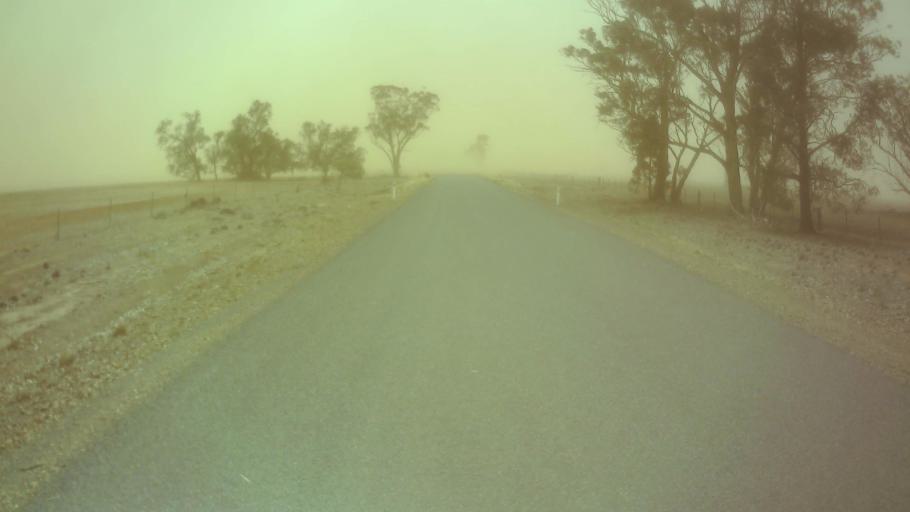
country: AU
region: New South Wales
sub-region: Weddin
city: Grenfell
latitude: -33.7140
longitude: 147.9078
